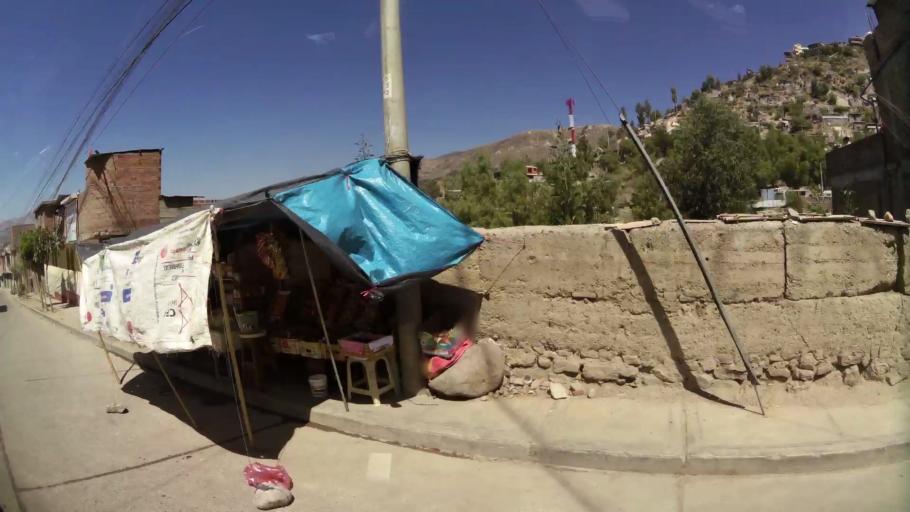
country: PE
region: Ayacucho
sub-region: Provincia de Huamanga
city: Ayacucho
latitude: -13.1644
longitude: -74.2358
